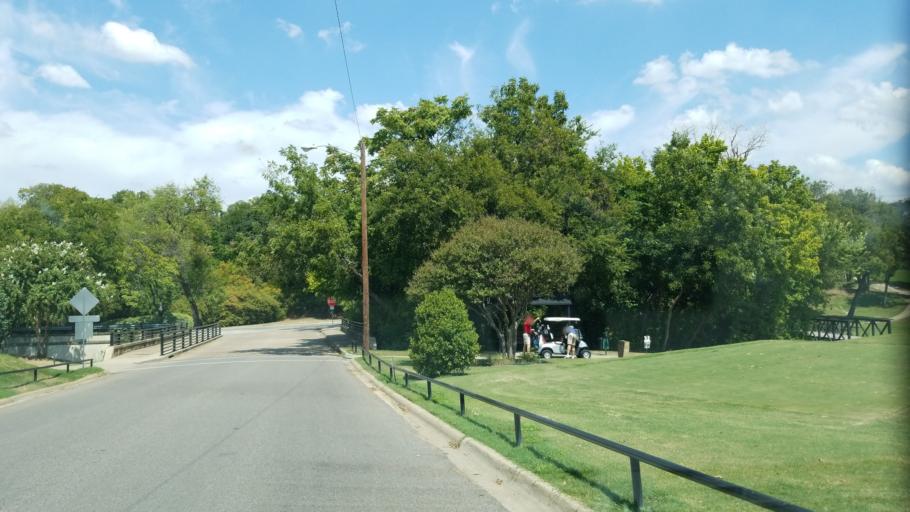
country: US
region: Texas
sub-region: Dallas County
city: Cockrell Hill
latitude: 32.7556
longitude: -96.8546
